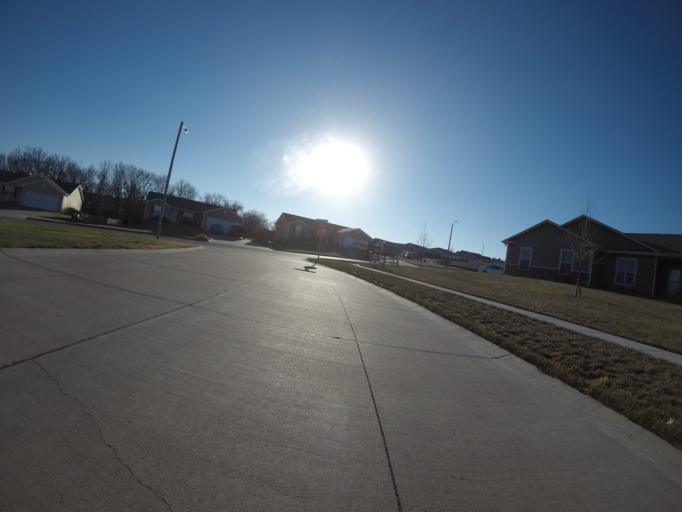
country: US
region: Kansas
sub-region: Riley County
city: Manhattan
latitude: 39.1829
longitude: -96.6459
